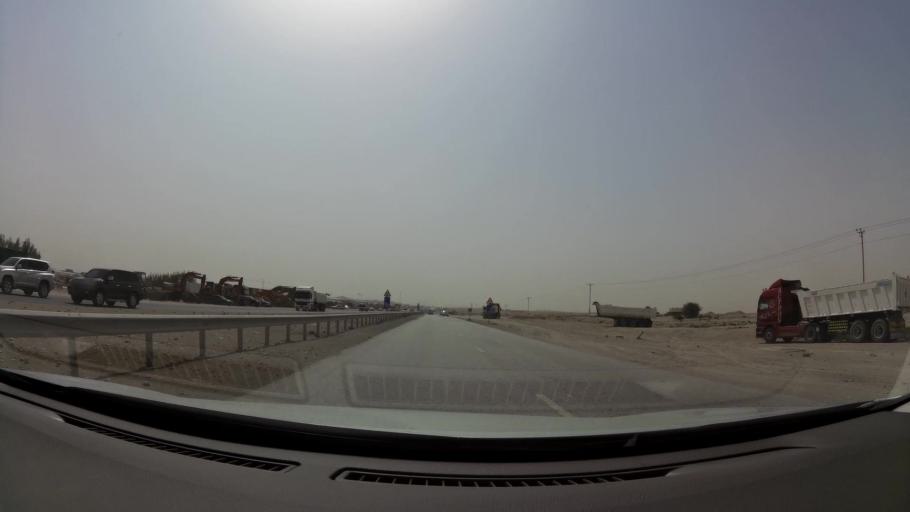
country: QA
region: Baladiyat ar Rayyan
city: Ar Rayyan
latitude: 25.2251
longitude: 51.3748
